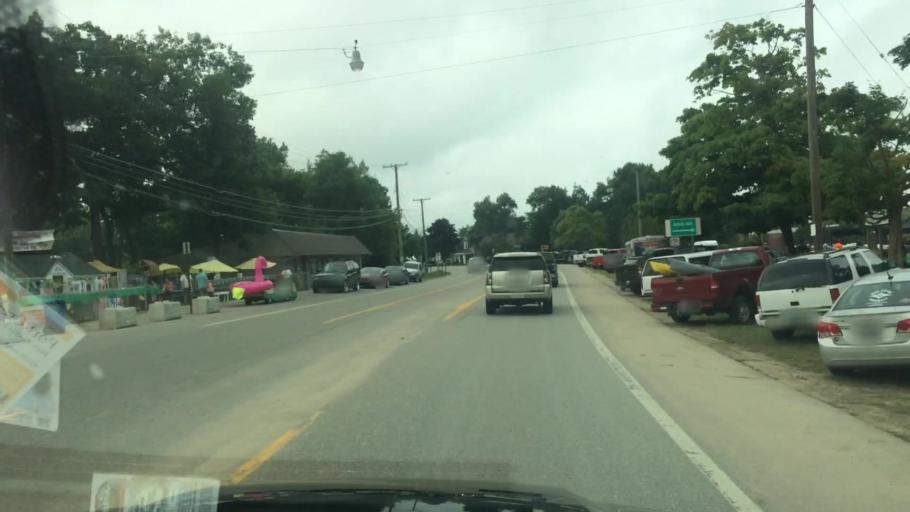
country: US
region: Michigan
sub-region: Huron County
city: Pigeon
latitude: 43.9467
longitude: -83.2716
